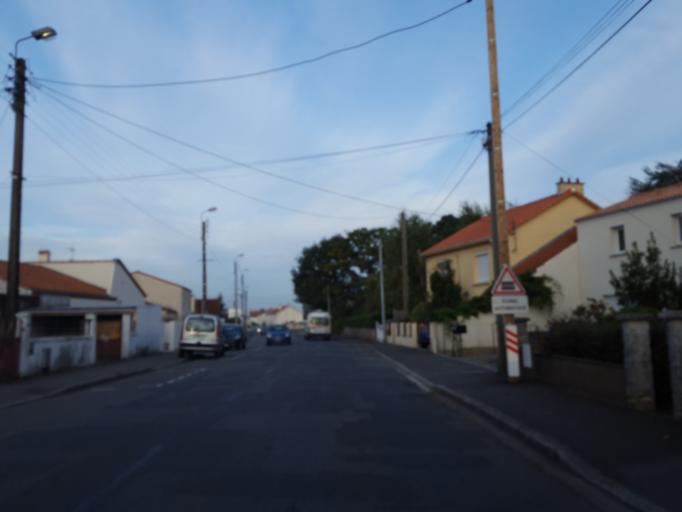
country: FR
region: Pays de la Loire
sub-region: Departement de la Loire-Atlantique
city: Saint-Sebastien-sur-Loire
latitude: 47.1994
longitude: -1.5017
